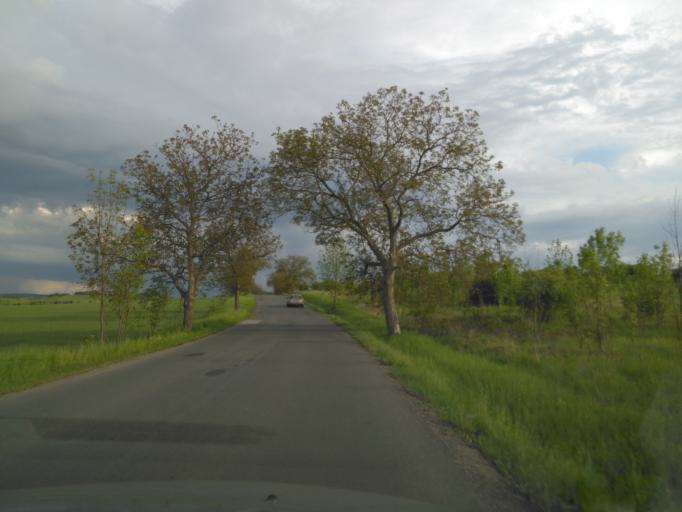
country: CZ
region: Central Bohemia
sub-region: Okres Beroun
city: Beroun
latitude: 49.9371
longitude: 14.0720
